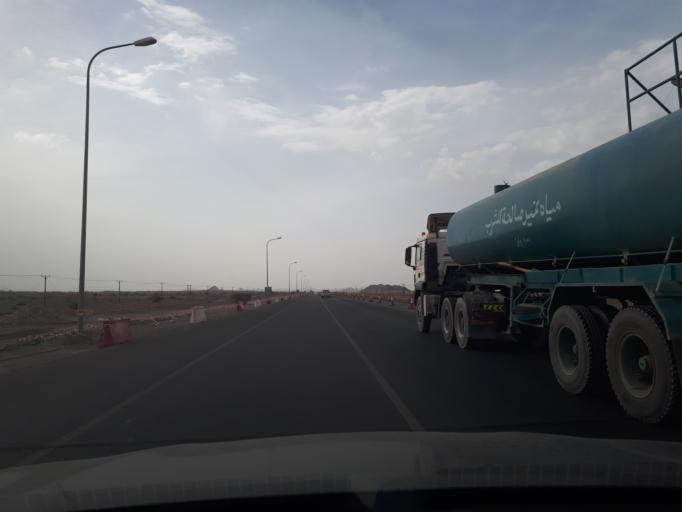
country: OM
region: Ash Sharqiyah
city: Al Qabil
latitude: 22.5412
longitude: 58.7264
